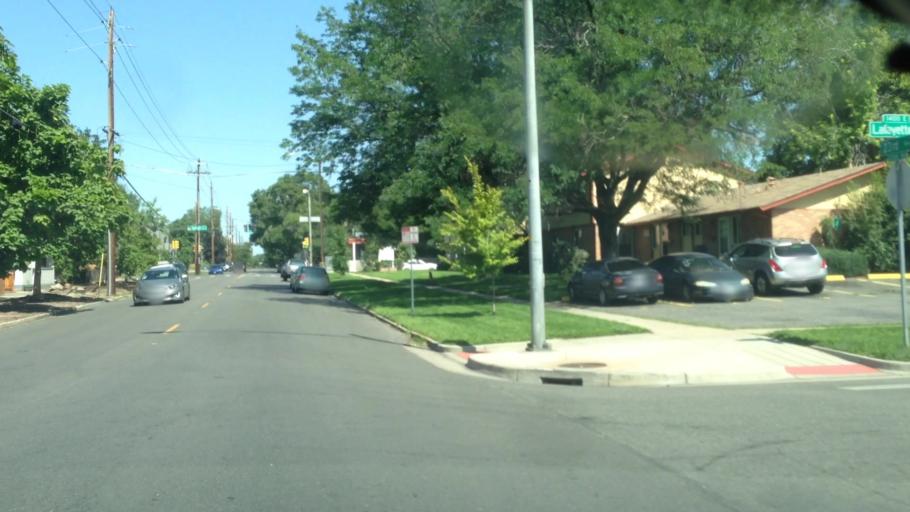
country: US
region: Colorado
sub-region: Denver County
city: Denver
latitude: 39.7507
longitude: -104.9710
